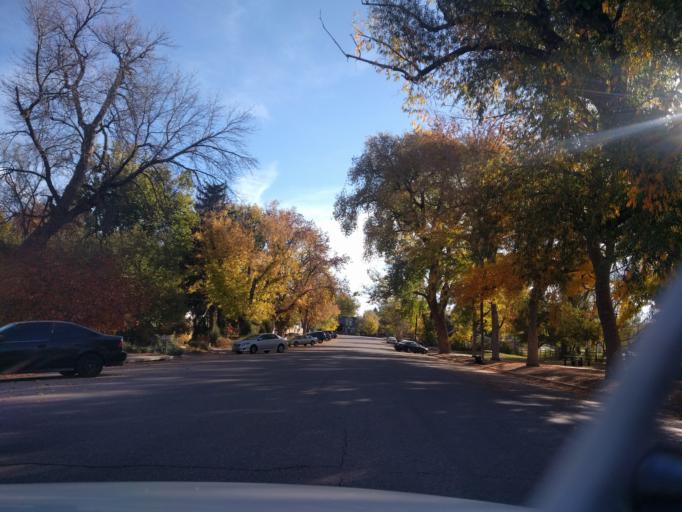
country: US
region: Colorado
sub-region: El Paso County
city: Colorado Springs
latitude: 38.8365
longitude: -104.8155
